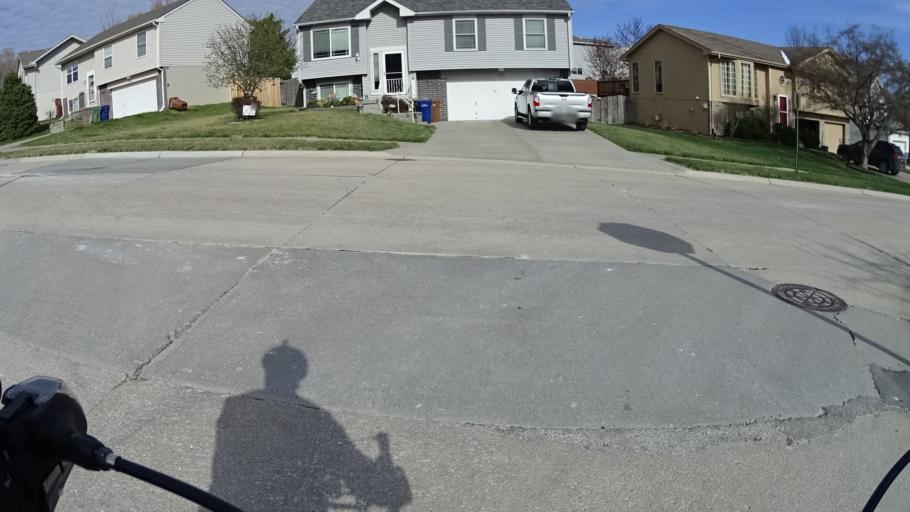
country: US
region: Nebraska
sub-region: Sarpy County
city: Offutt Air Force Base
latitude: 41.1098
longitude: -95.9601
